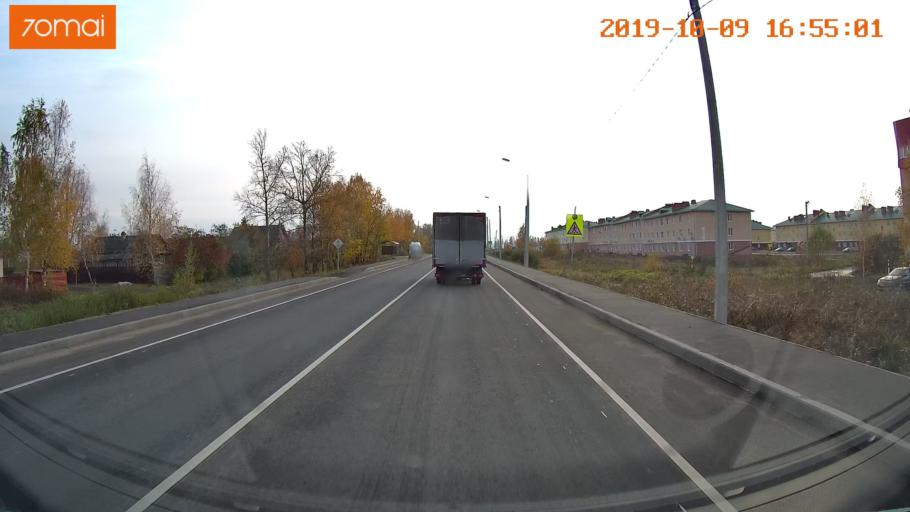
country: RU
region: Ivanovo
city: Privolzhsk
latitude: 57.3704
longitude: 41.2767
